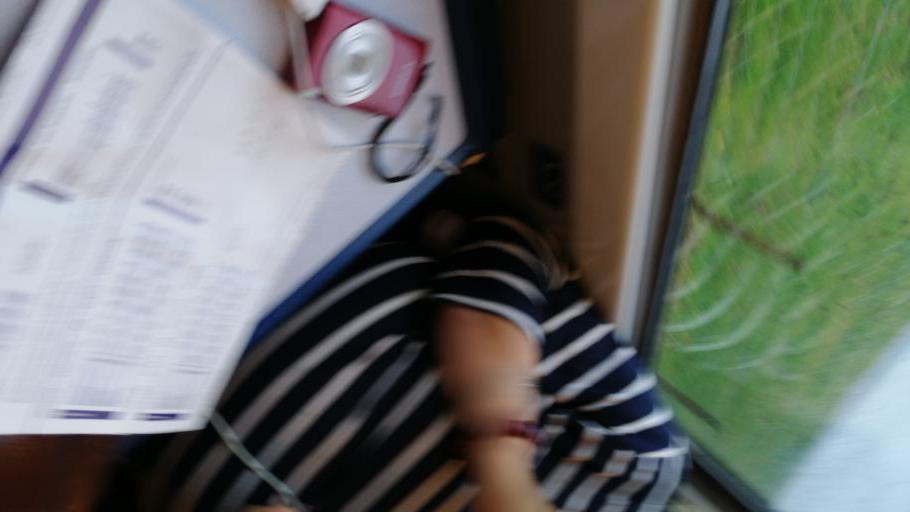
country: GB
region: Scotland
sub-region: Highland
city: Brora
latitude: 58.0570
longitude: -3.8061
